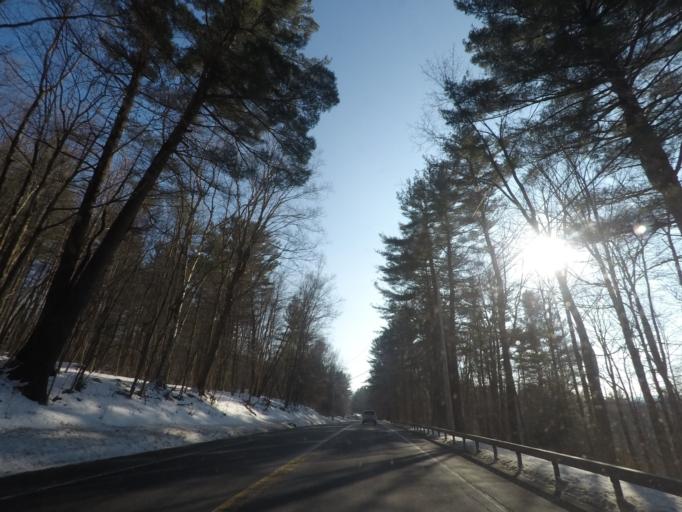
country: US
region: Massachusetts
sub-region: Berkshire County
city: Richmond
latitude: 42.4942
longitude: -73.3719
